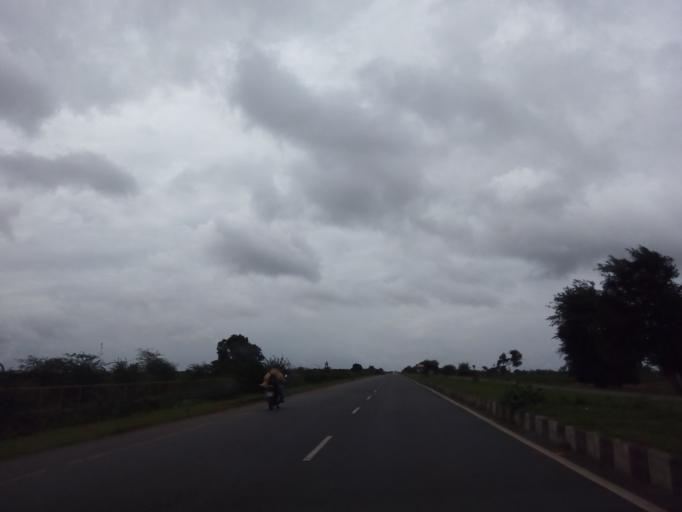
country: IN
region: Karnataka
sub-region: Haveri
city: Haveri
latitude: 14.7494
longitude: 75.4508
